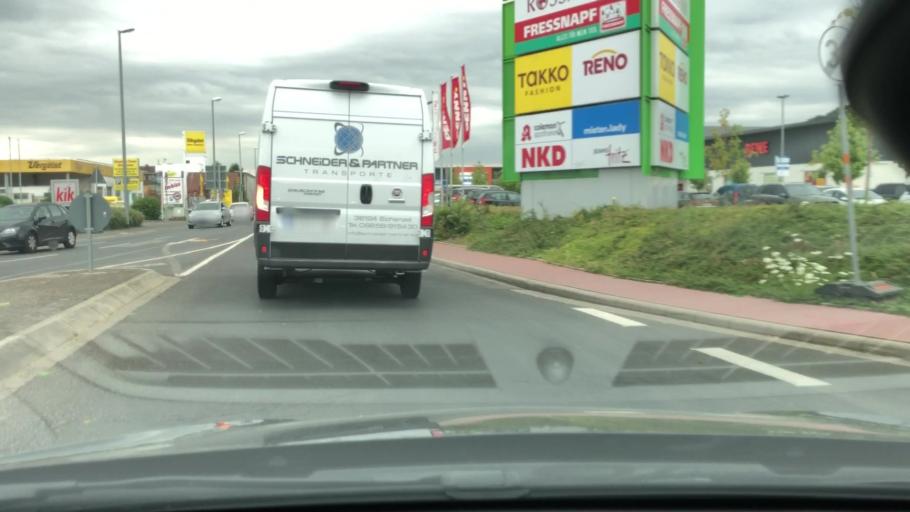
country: DE
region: Hesse
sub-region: Regierungsbezirk Darmstadt
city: Gelnhausen
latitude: 50.2020
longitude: 9.1777
